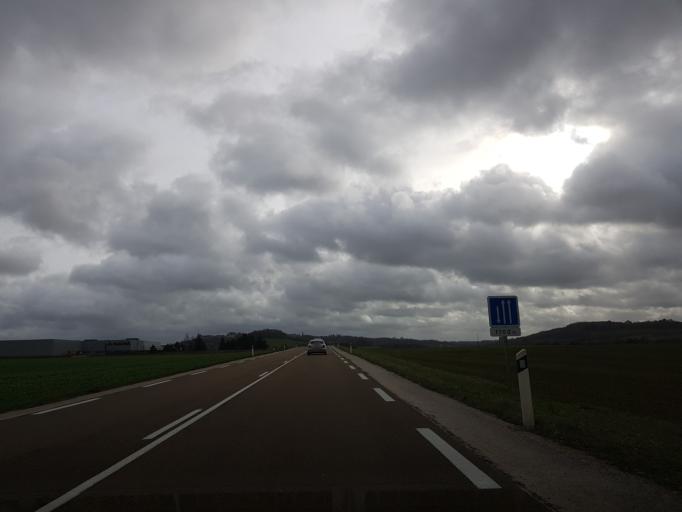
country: FR
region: Champagne-Ardenne
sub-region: Departement de la Haute-Marne
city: Langres
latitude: 47.8923
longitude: 5.3145
